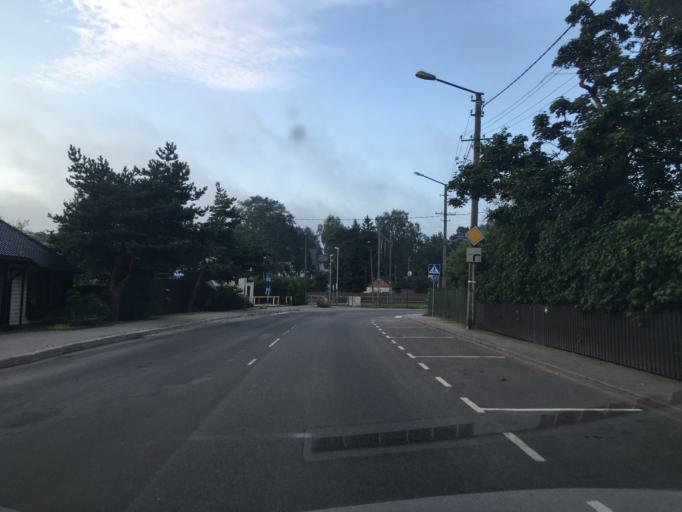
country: EE
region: Harju
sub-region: Tallinna linn
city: Tallinn
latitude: 59.3892
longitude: 24.7021
